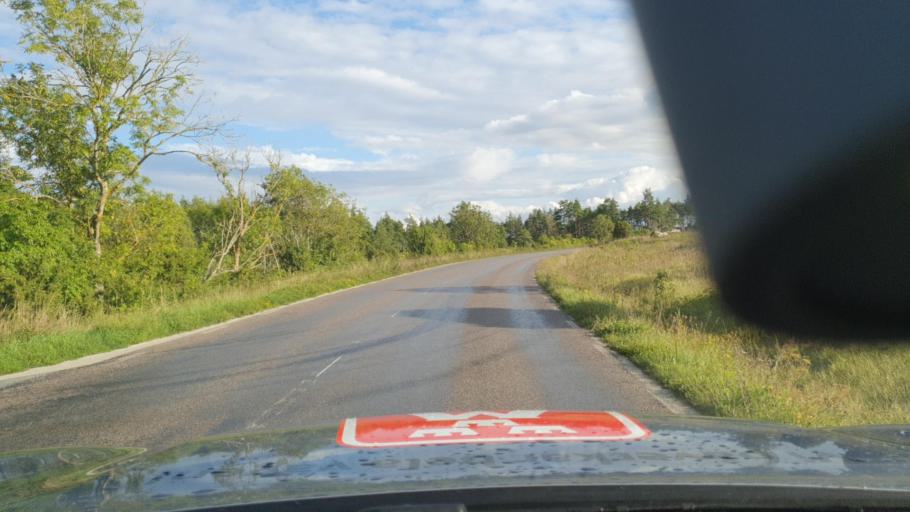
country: SE
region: Gotland
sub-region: Gotland
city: Slite
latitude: 57.6717
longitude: 18.7740
